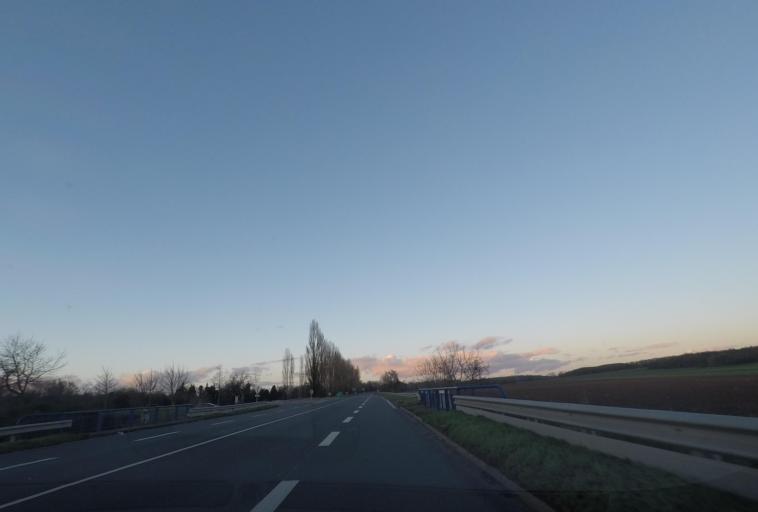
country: FR
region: Ile-de-France
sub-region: Departement de l'Essonne
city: Vert-le-Grand
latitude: 48.5716
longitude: 2.3644
